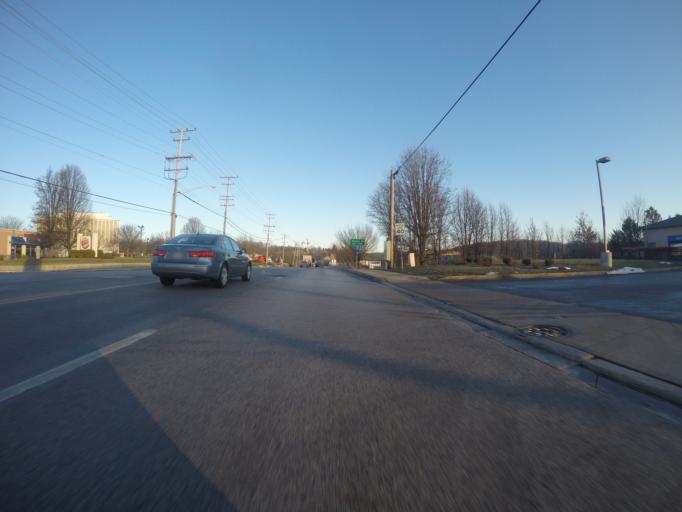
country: US
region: Maryland
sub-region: Baltimore County
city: Hunt Valley
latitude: 39.4929
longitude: -76.6490
